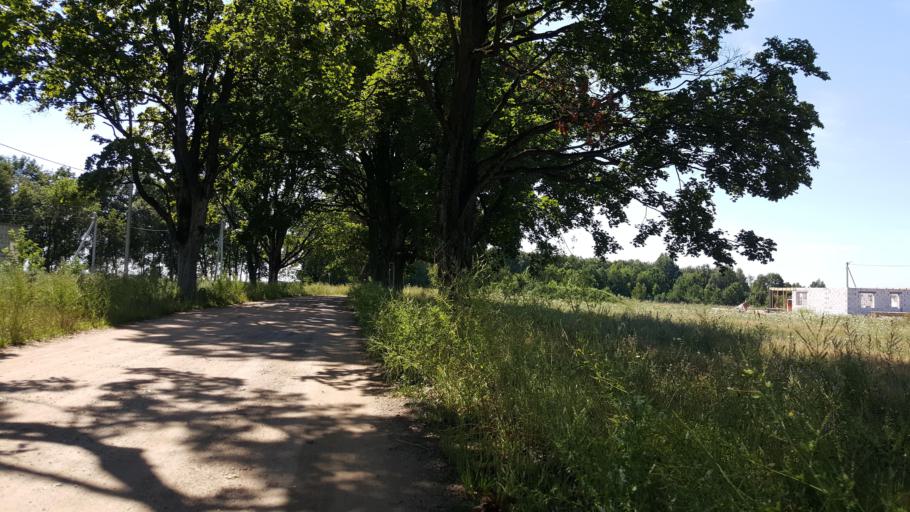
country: BY
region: Brest
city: Charnawchytsy
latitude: 52.2665
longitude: 23.7645
